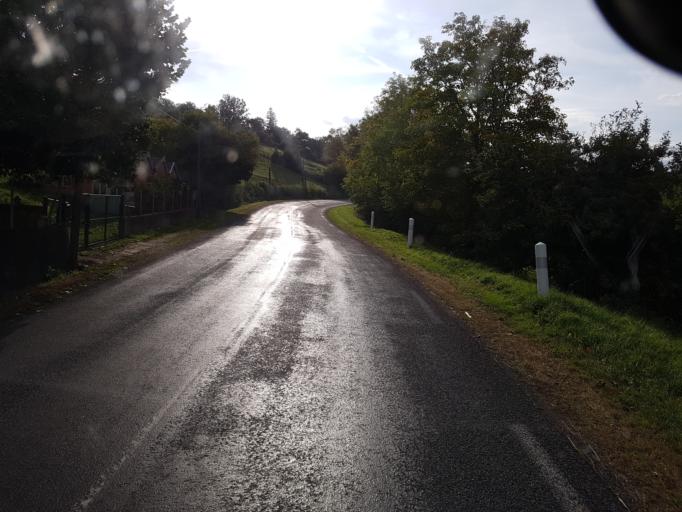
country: FR
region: Bourgogne
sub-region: Departement de Saone-et-Loire
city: Chauffailles
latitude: 46.2318
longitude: 4.4182
